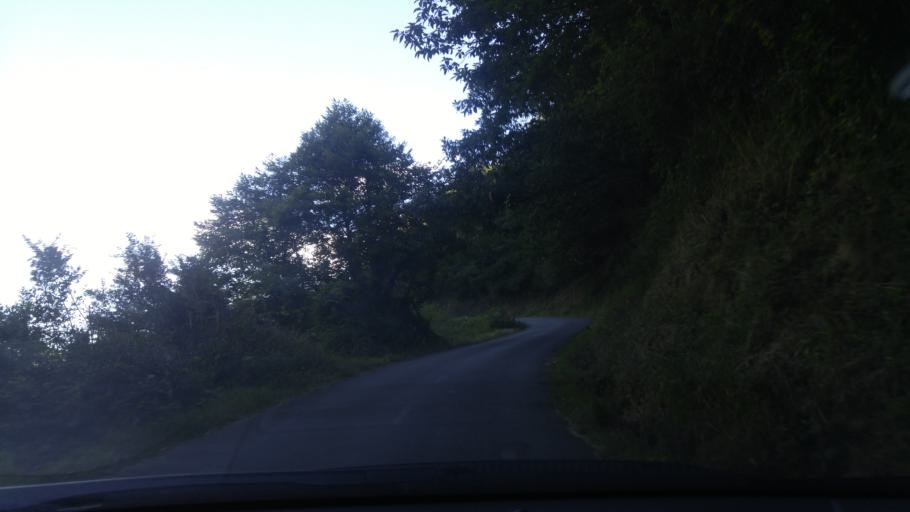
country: ES
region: Asturias
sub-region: Province of Asturias
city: Barzana
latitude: 43.1689
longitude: -5.9837
